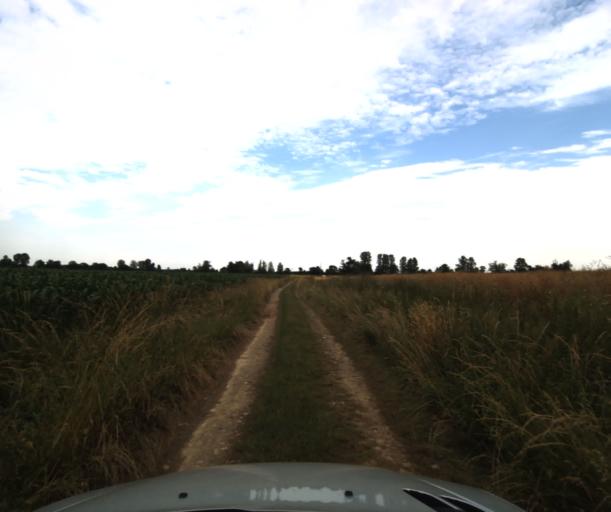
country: FR
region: Midi-Pyrenees
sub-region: Departement de la Haute-Garonne
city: Labastidette
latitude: 43.4773
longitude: 1.2188
